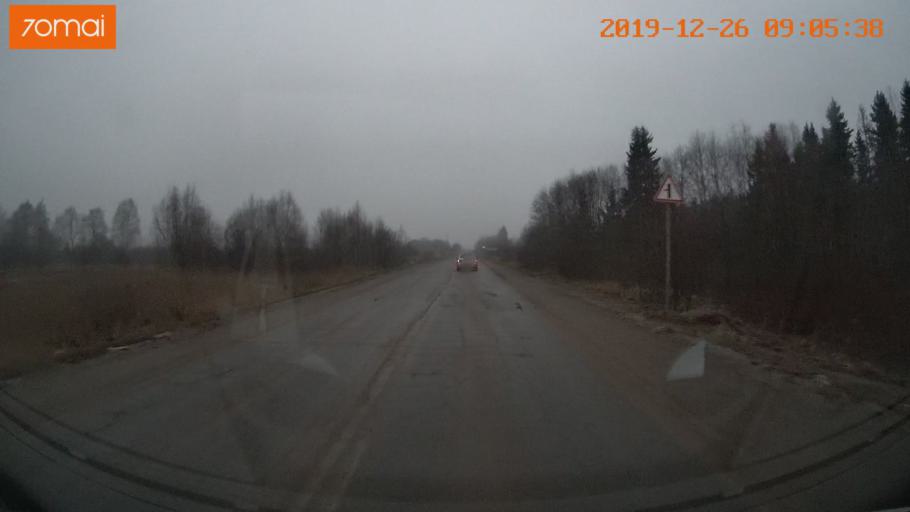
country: RU
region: Vologda
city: Gryazovets
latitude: 58.8276
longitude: 40.2571
